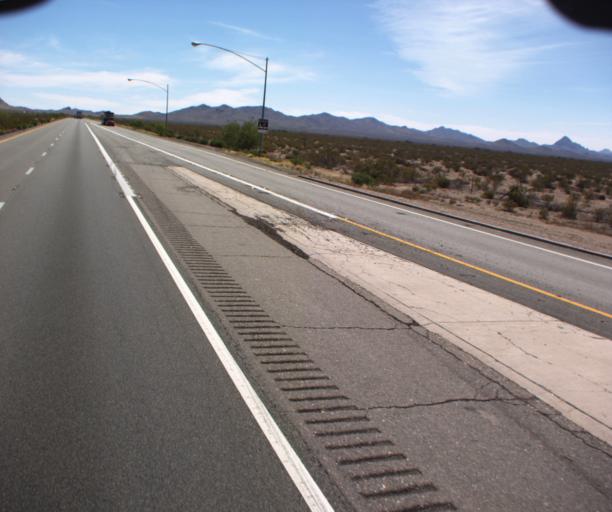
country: US
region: New Mexico
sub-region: Hidalgo County
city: Lordsburg
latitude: 32.2363
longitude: -109.0873
